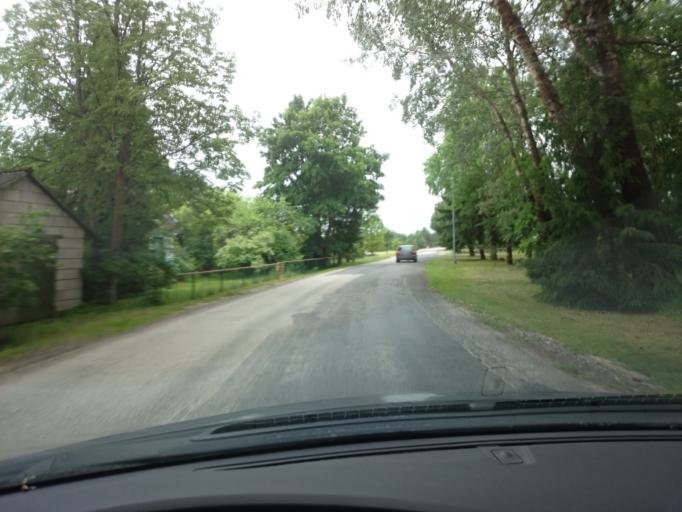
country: EE
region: Saare
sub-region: Orissaare vald
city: Orissaare
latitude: 58.6036
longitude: 23.2361
